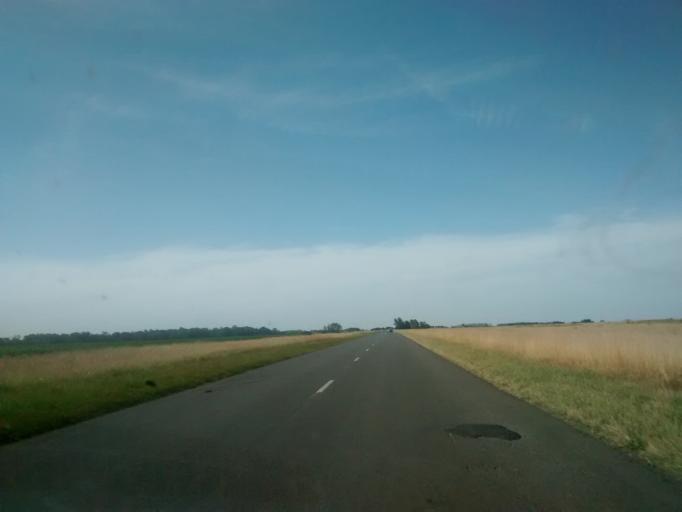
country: AR
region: Buenos Aires
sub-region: Partido de Ayacucho
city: Ayacucho
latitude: -37.4737
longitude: -58.4785
